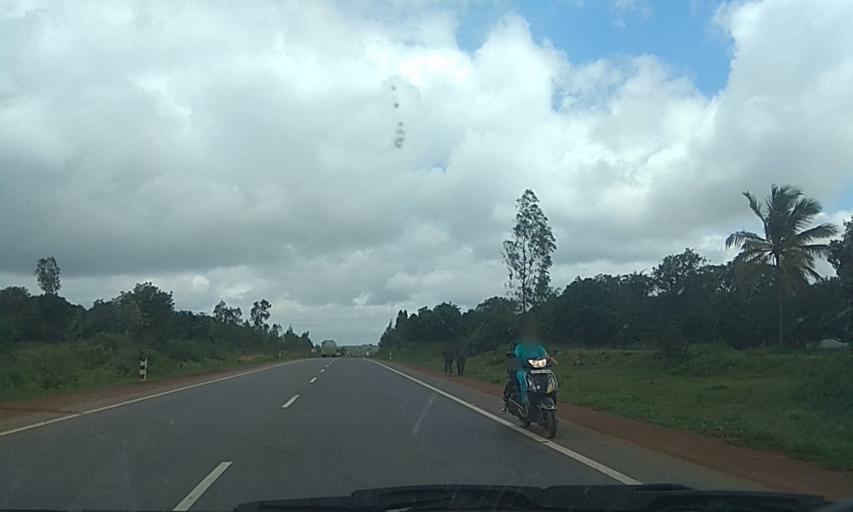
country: IN
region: Karnataka
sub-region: Dharwad
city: Hubli
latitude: 15.4474
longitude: 74.9689
